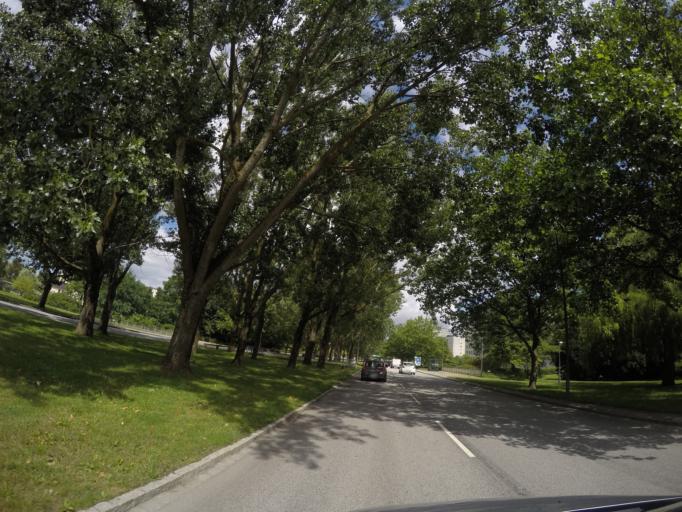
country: SE
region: Skane
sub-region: Malmo
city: Malmoe
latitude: 55.5767
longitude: 12.9933
